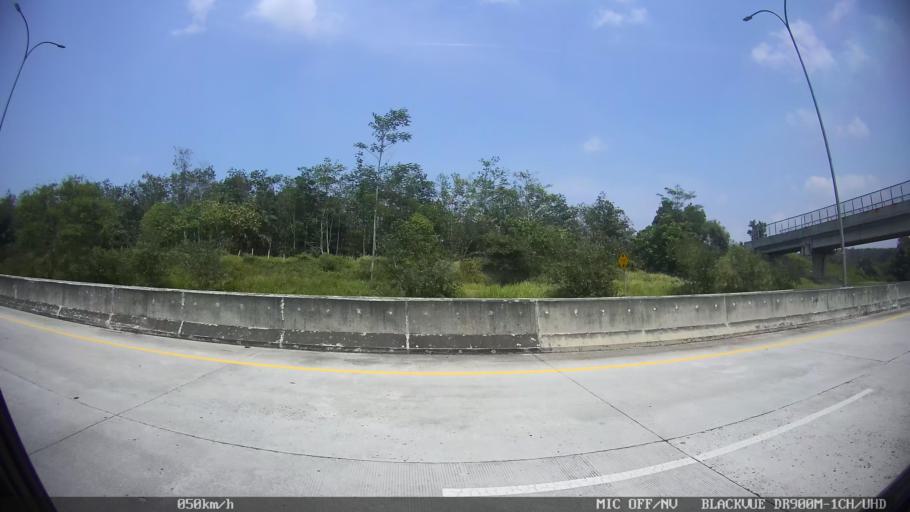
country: ID
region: Lampung
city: Kedaton
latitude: -5.3689
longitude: 105.3268
